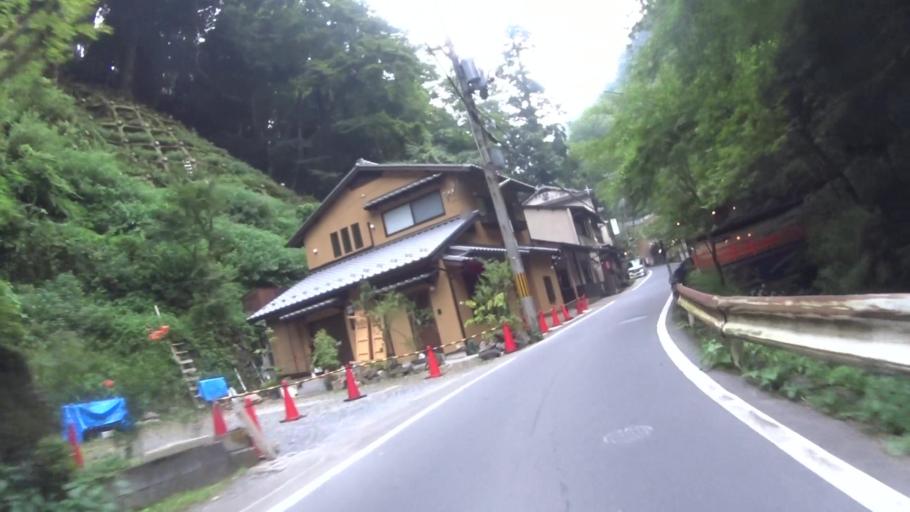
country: JP
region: Kyoto
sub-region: Kyoto-shi
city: Kamigyo-ku
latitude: 35.1209
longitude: 135.7627
